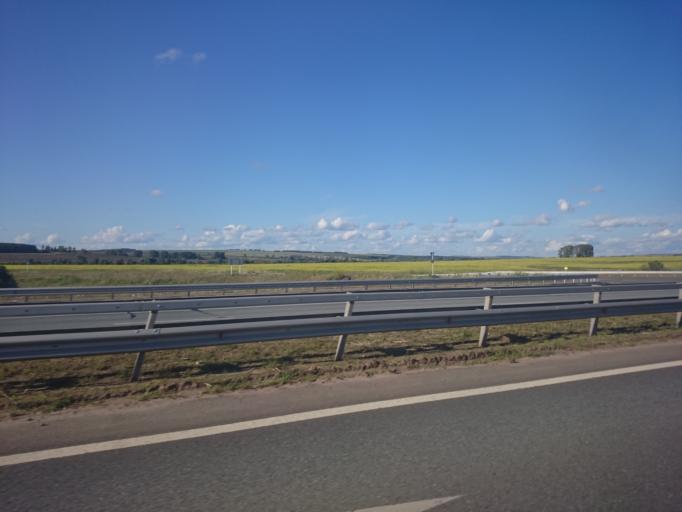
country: RU
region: Tatarstan
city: Nizhnekamsk
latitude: 55.7122
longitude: 51.6232
